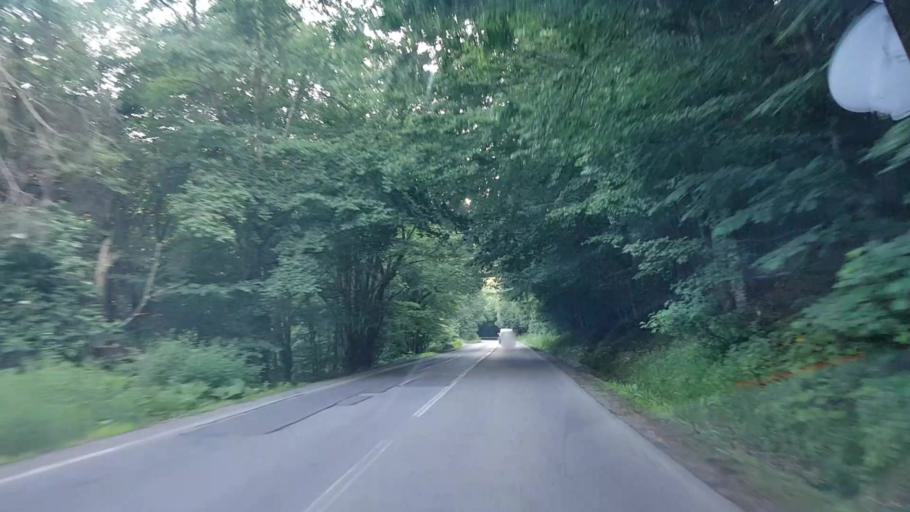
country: RO
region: Harghita
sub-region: Comuna Praid
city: Ocna de Sus
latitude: 46.5831
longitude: 25.2423
